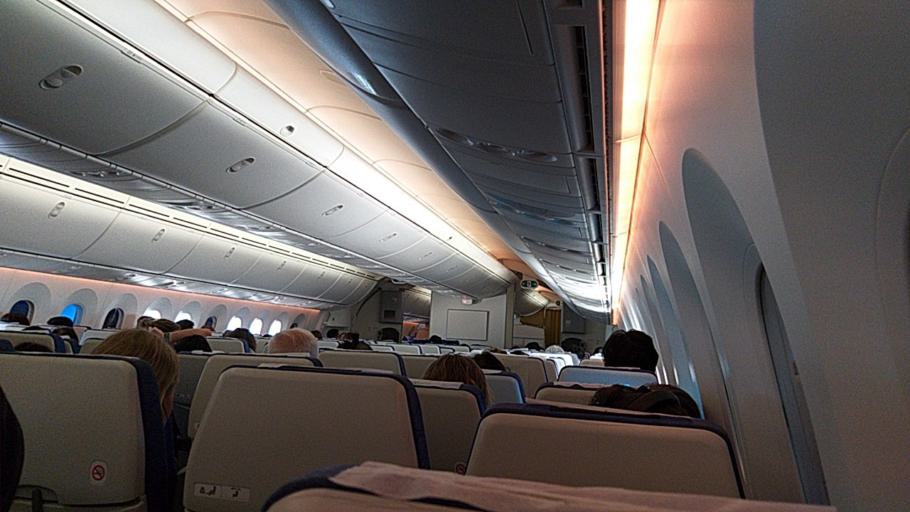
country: SG
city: Singapore
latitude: 1.3542
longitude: 103.9929
